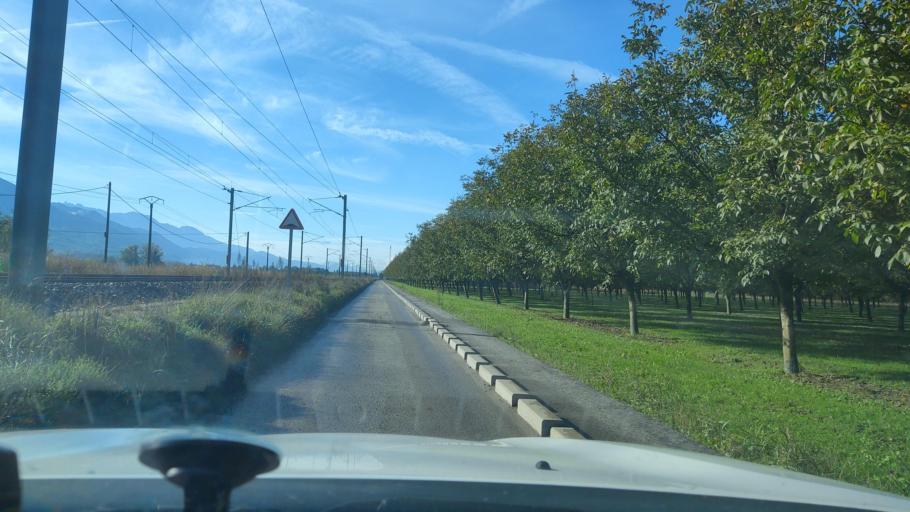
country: FR
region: Rhone-Alpes
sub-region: Departement de l'Isere
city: Pontcharra
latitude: 45.4607
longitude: 6.0270
